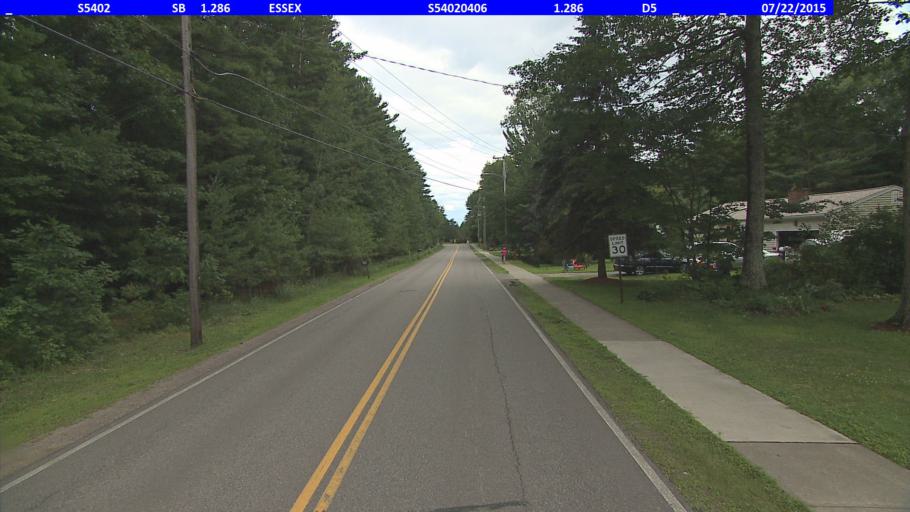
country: US
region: Vermont
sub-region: Chittenden County
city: Jericho
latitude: 44.4968
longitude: -73.0495
